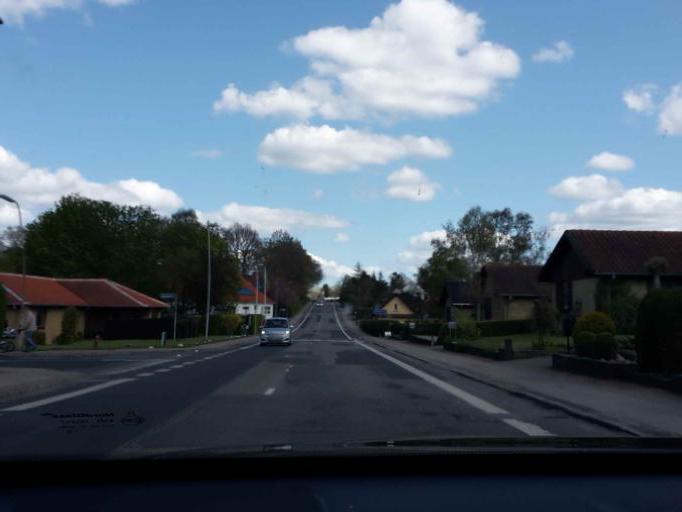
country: DK
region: South Denmark
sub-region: Odense Kommune
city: Odense
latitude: 55.4104
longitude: 10.3209
